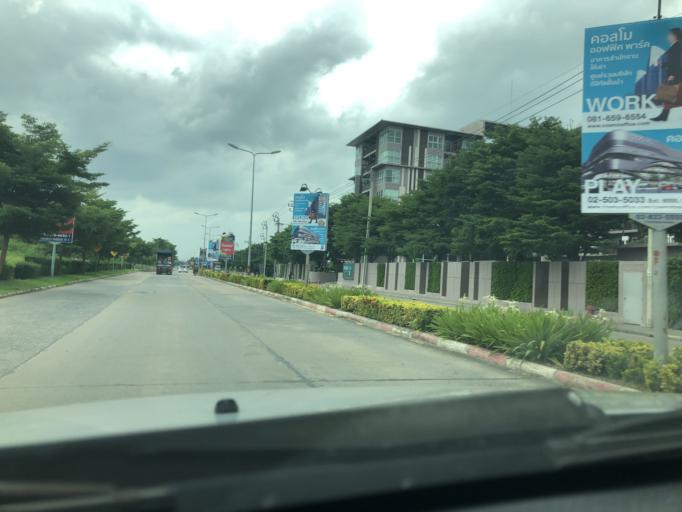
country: TH
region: Bangkok
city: Don Mueang
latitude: 13.9231
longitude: 100.5451
